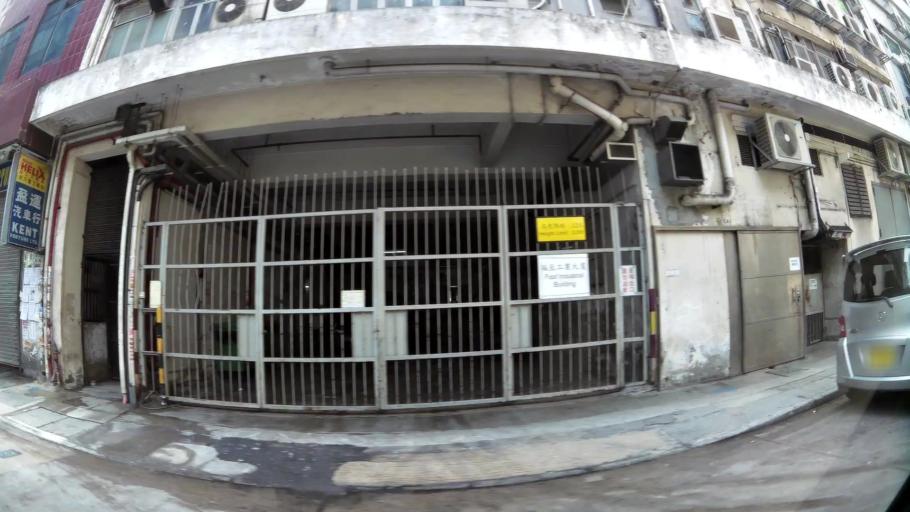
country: HK
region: Sham Shui Po
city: Sham Shui Po
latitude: 22.3388
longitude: 114.1480
